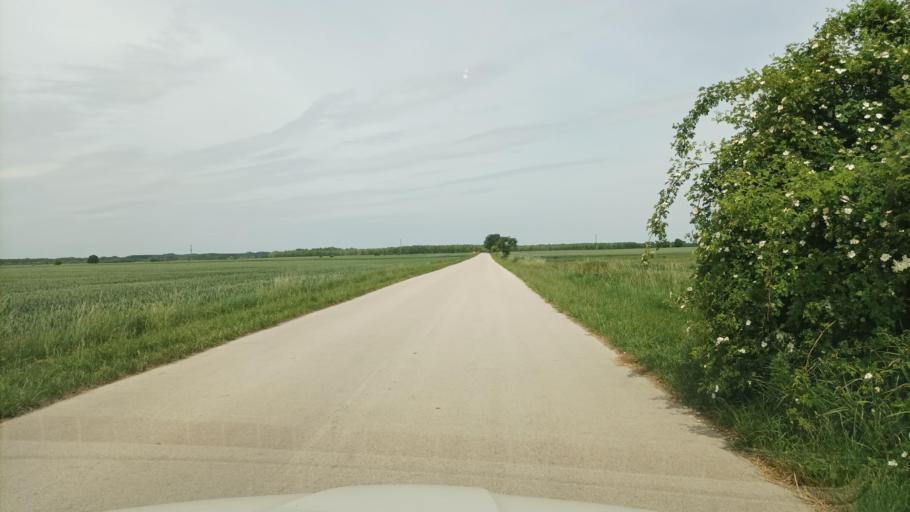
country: HU
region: Pest
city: Rackeve
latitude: 47.1153
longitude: 18.9194
